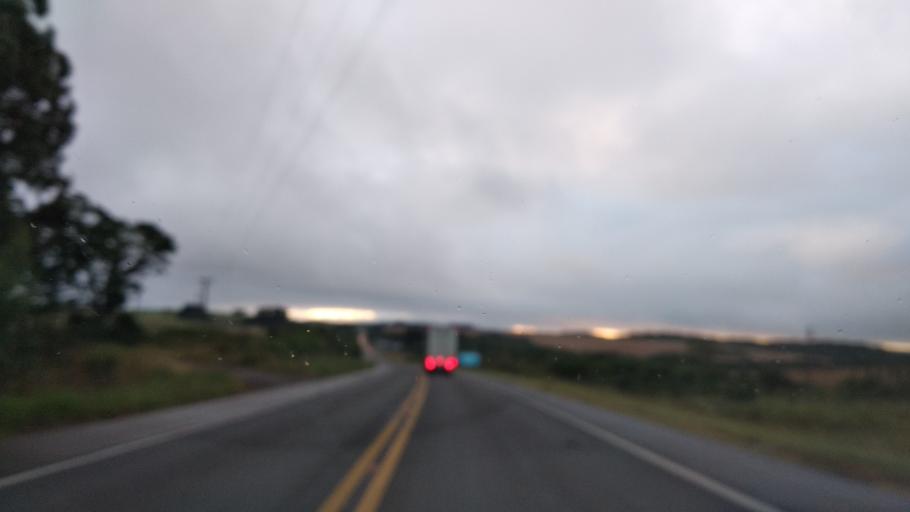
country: BR
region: Santa Catarina
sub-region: Campos Novos
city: Campos Novos
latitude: -27.3897
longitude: -51.1214
